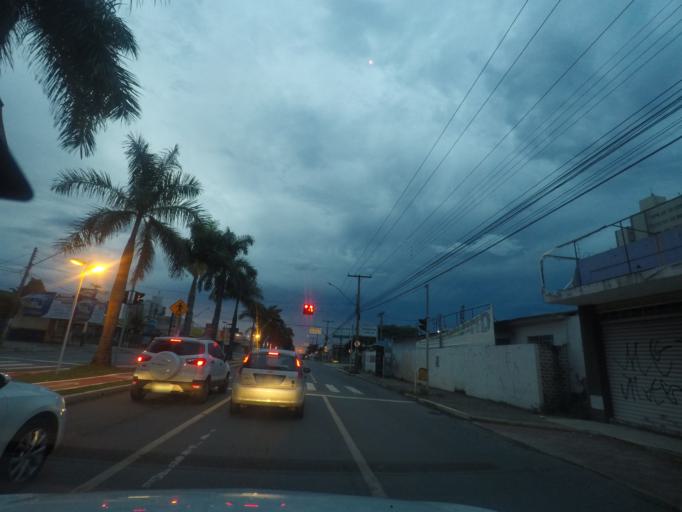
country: BR
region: Goias
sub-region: Goiania
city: Goiania
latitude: -16.7153
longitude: -49.2807
